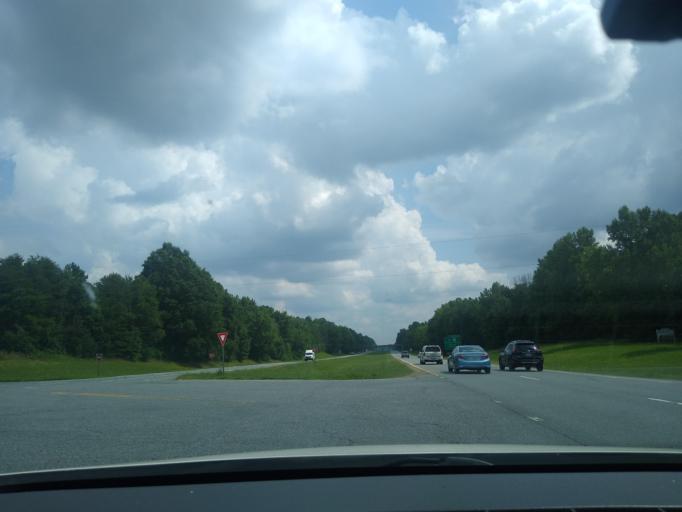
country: US
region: North Carolina
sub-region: Guilford County
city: Pleasant Garden
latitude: 36.0198
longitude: -79.7635
